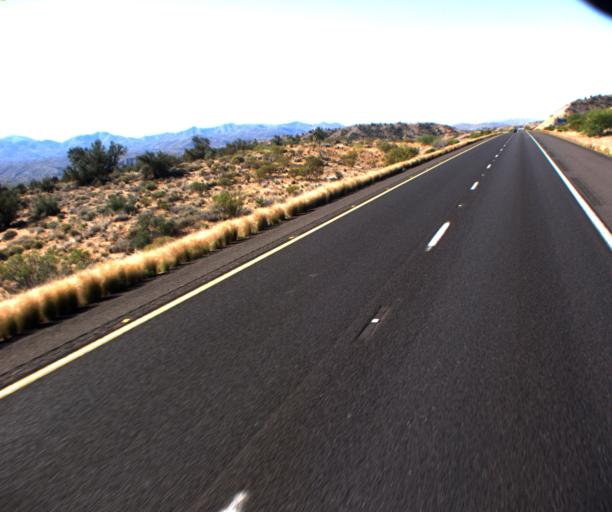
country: US
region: Arizona
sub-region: Mohave County
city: Kingman
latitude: 35.0897
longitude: -113.6663
